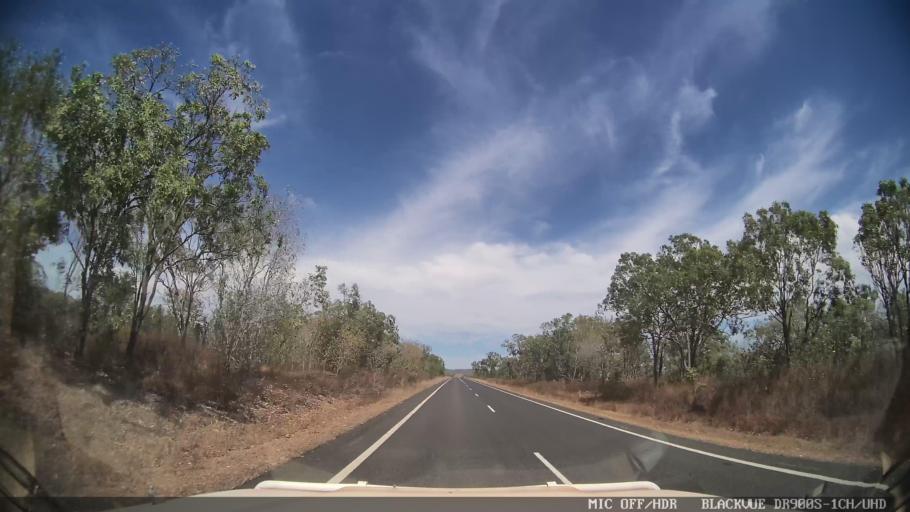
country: AU
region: Queensland
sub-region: Cook
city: Cooktown
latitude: -15.8820
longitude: 144.8594
